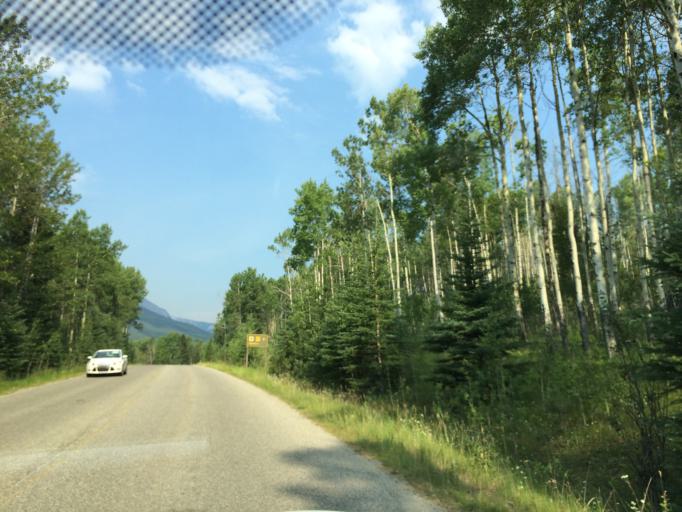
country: CA
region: Alberta
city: Banff
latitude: 51.1796
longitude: -115.7183
